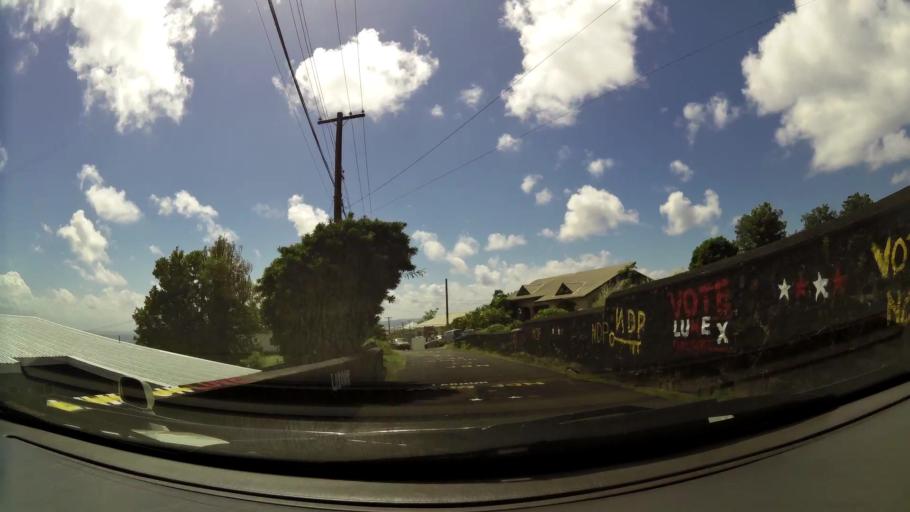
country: VC
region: Saint George
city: Kingstown
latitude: 13.1460
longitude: -61.2226
